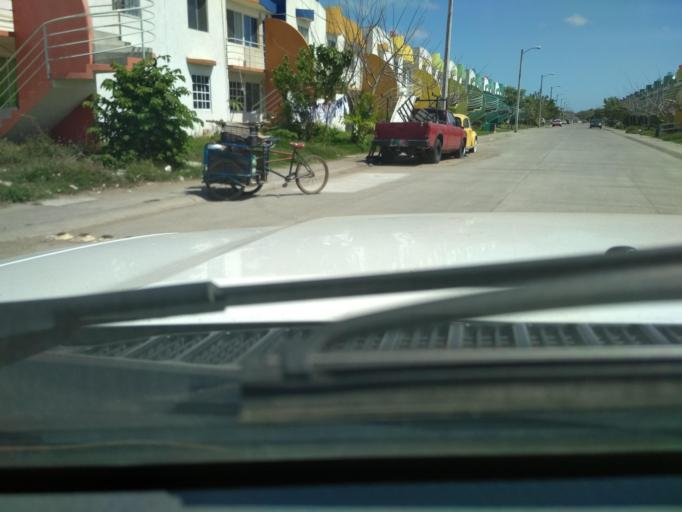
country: MX
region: Veracruz
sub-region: Veracruz
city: Las Amapolas
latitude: 19.1345
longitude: -96.2094
